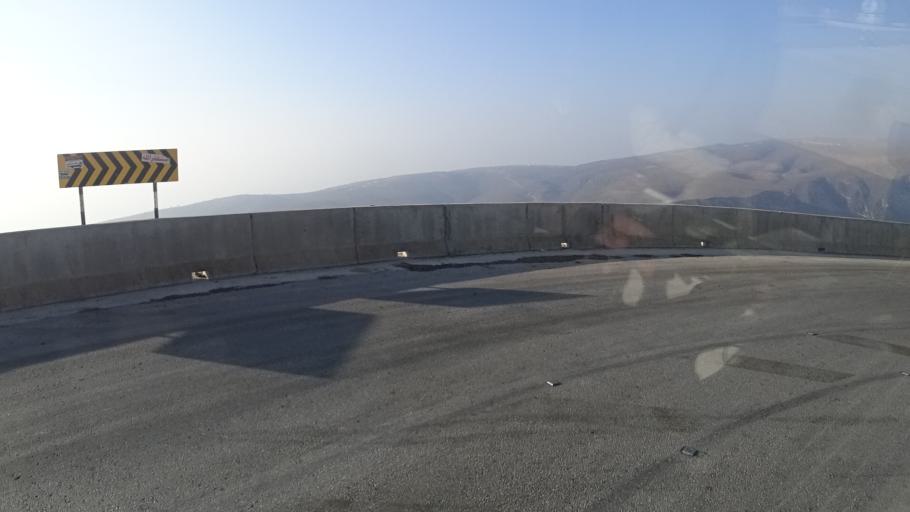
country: YE
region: Al Mahrah
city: Hawf
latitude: 16.7550
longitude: 53.2368
